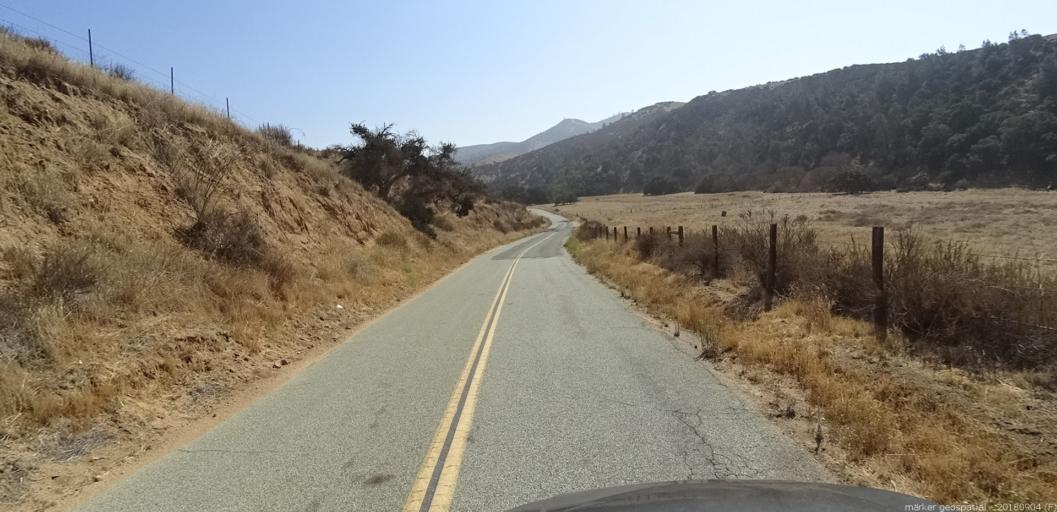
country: US
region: California
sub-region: Monterey County
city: Soledad
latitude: 36.5129
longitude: -121.3493
